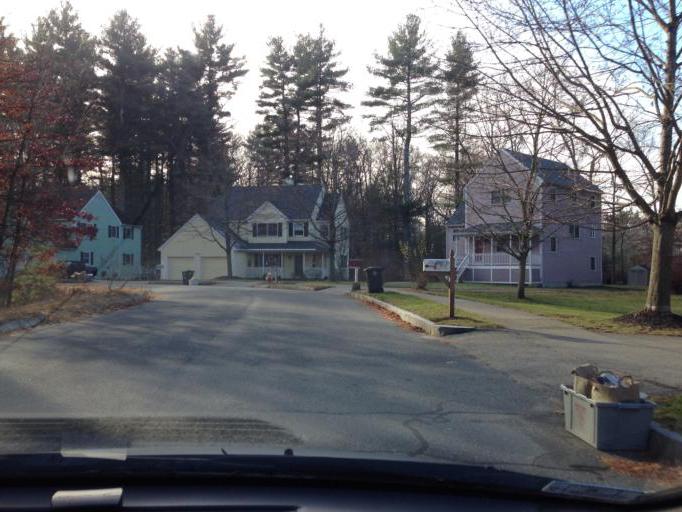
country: US
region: Massachusetts
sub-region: Middlesex County
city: Bedford
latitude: 42.4987
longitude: -71.3024
